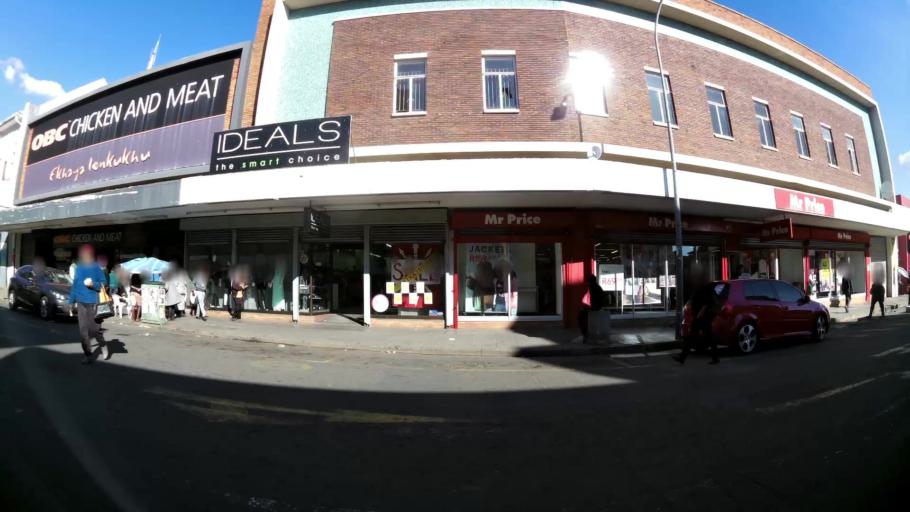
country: ZA
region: Northern Cape
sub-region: Frances Baard District Municipality
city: Kimberley
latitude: -28.7400
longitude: 24.7632
